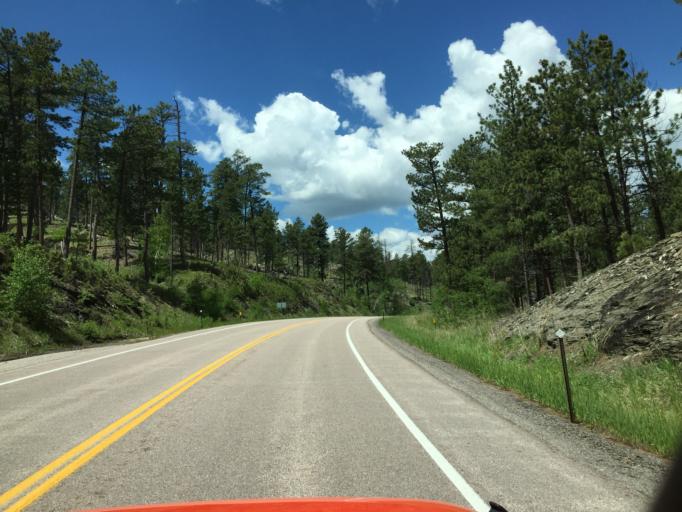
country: US
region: South Dakota
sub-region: Custer County
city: Custer
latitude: 43.8953
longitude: -103.5160
